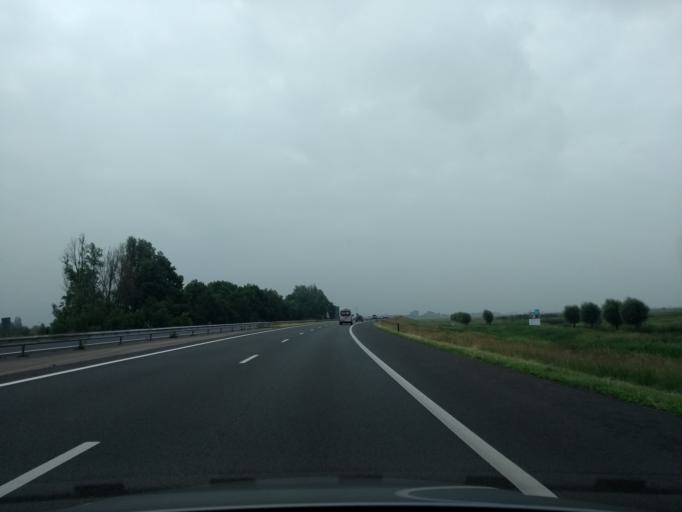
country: NL
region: Friesland
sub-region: Sudwest Fryslan
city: Oppenhuizen
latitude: 53.0160
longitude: 5.6850
